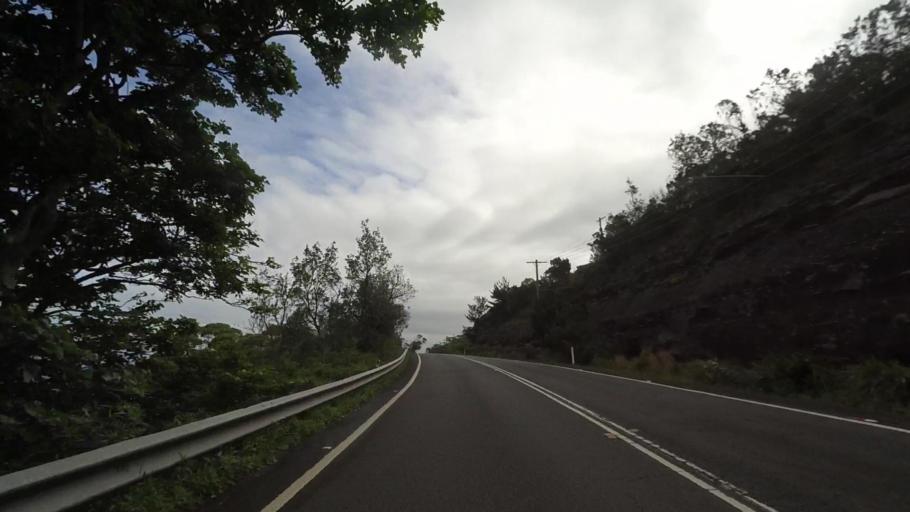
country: AU
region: New South Wales
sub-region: Wollongong
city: Helensburgh
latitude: -34.2161
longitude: 151.0047
